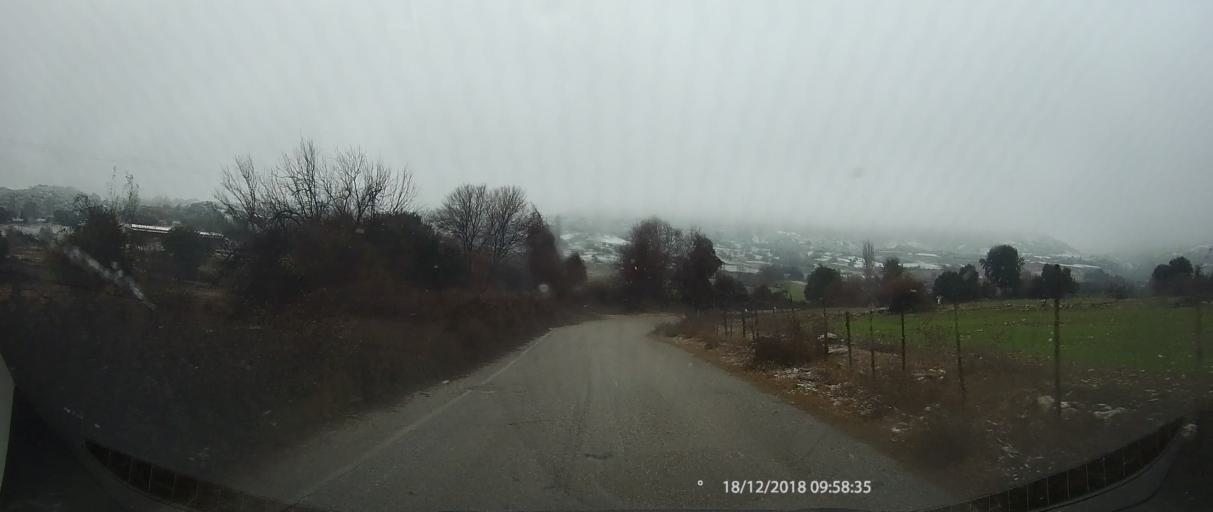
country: GR
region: Thessaly
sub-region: Nomos Larisis
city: Livadi
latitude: 40.0279
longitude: 22.2419
